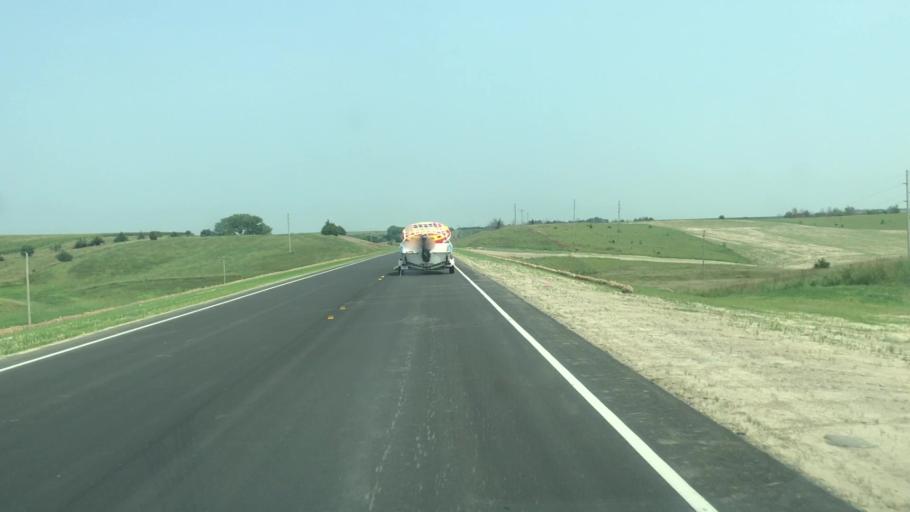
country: US
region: Nebraska
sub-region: Sherman County
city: Loup City
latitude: 41.2634
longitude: -98.9249
